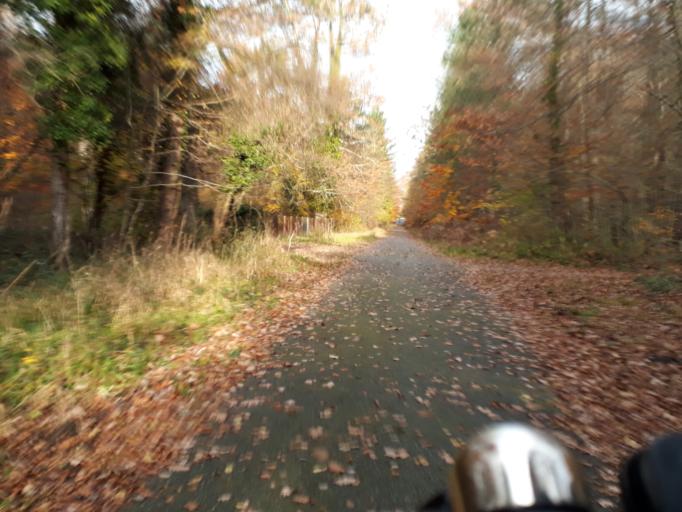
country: FR
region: Ile-de-France
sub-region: Departement de Seine-et-Marne
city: Bois-le-Roi
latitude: 48.4633
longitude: 2.6862
